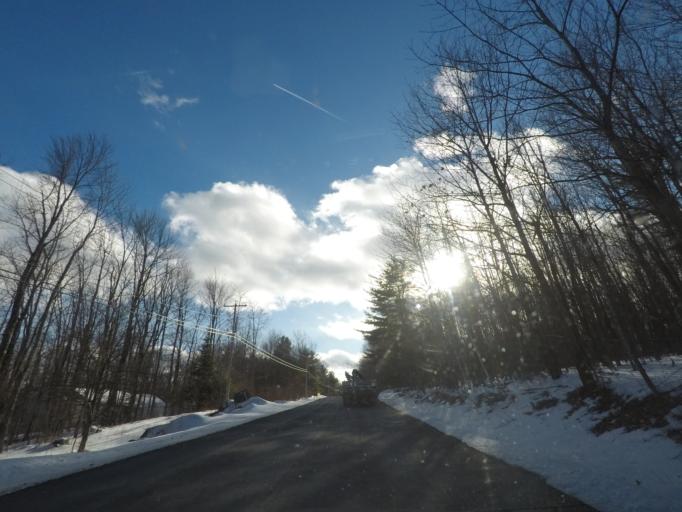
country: US
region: New York
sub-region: Rensselaer County
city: Hoosick Falls
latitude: 42.7816
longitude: -73.4208
